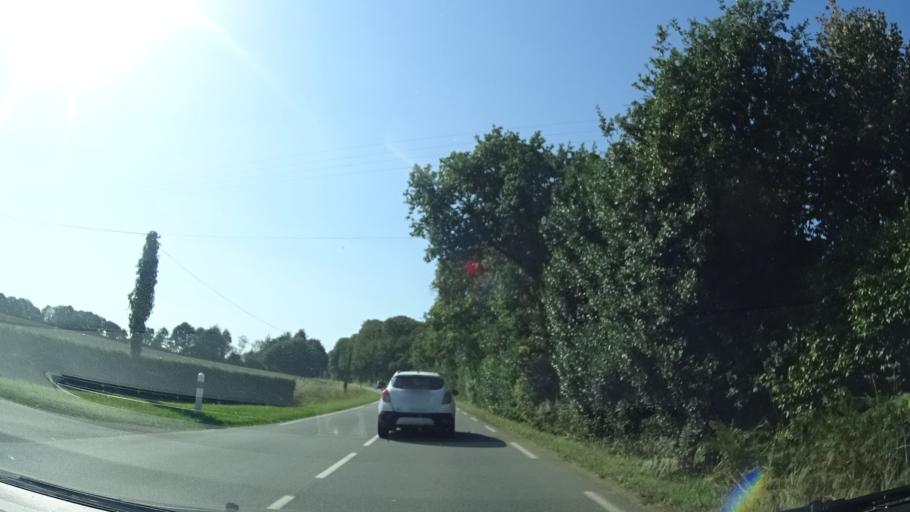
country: FR
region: Brittany
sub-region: Departement du Finistere
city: Plonevez-Porzay
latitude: 48.0985
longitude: -4.2553
